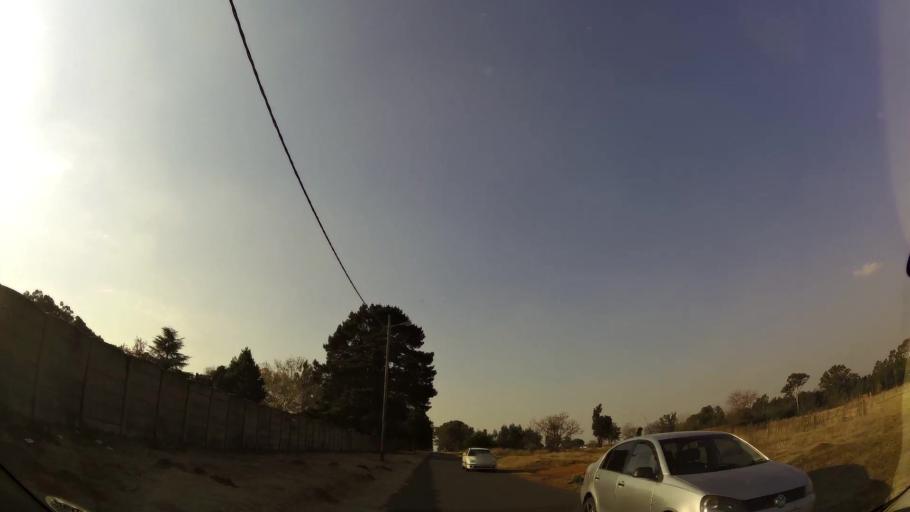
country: ZA
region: Gauteng
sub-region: Ekurhuleni Metropolitan Municipality
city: Benoni
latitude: -26.1491
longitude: 28.3664
